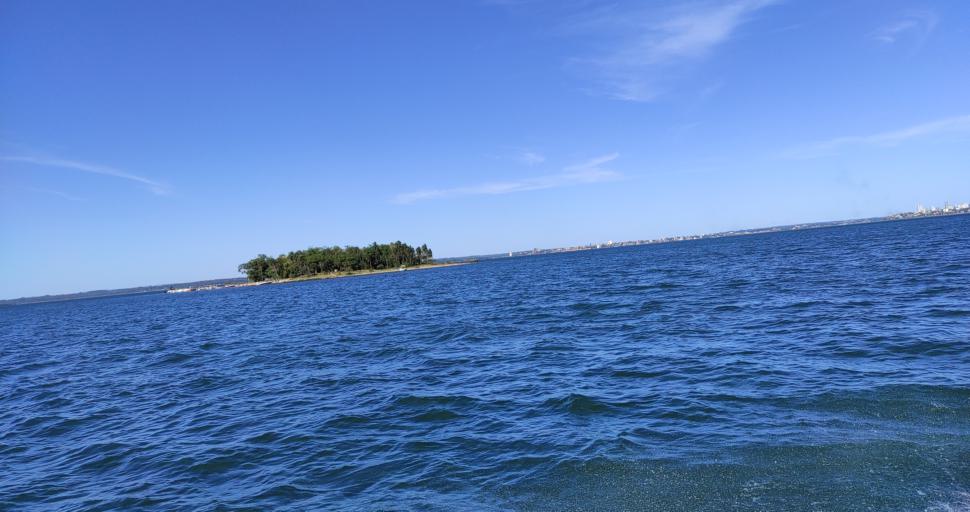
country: PY
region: Itapua
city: San Juan del Parana
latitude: -27.3418
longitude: -55.9536
